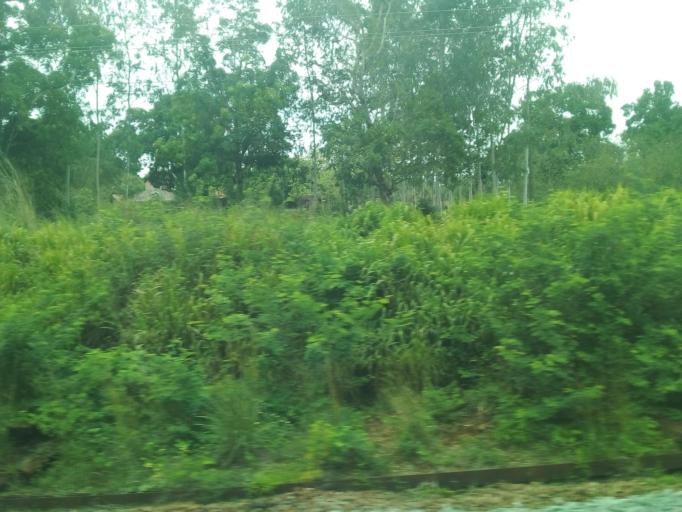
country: BR
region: Maranhao
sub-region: Santa Ines
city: Santa Ines
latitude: -3.6998
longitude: -45.4363
